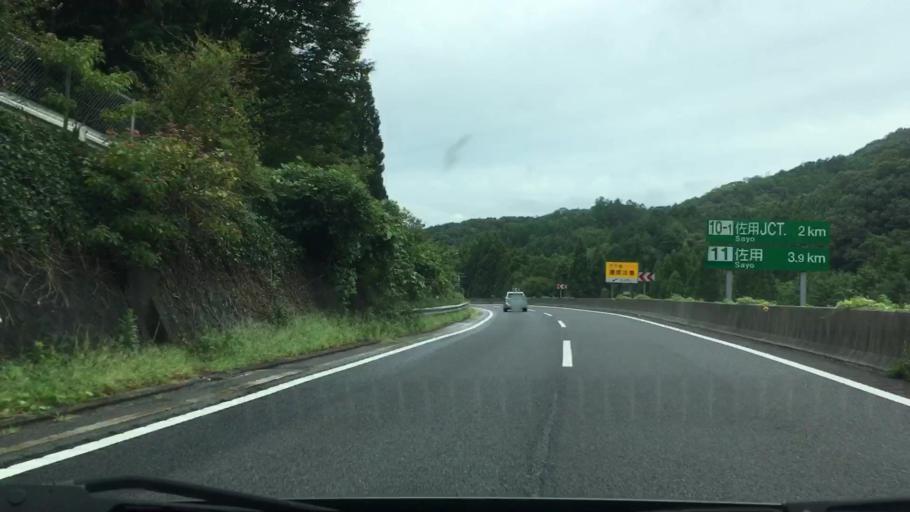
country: JP
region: Hyogo
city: Yamazakicho-nakabirose
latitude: 35.0353
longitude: 134.4066
